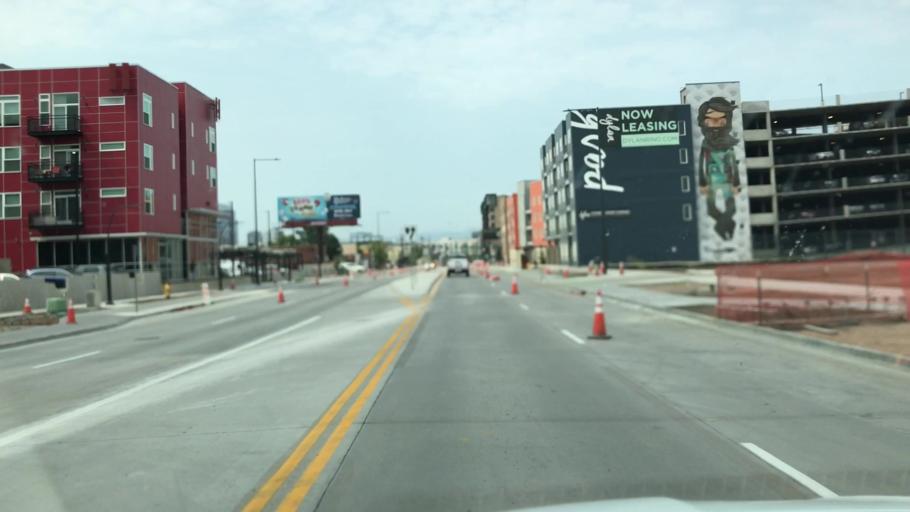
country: US
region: Colorado
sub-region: Denver County
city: Denver
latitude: 39.7684
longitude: -104.9814
